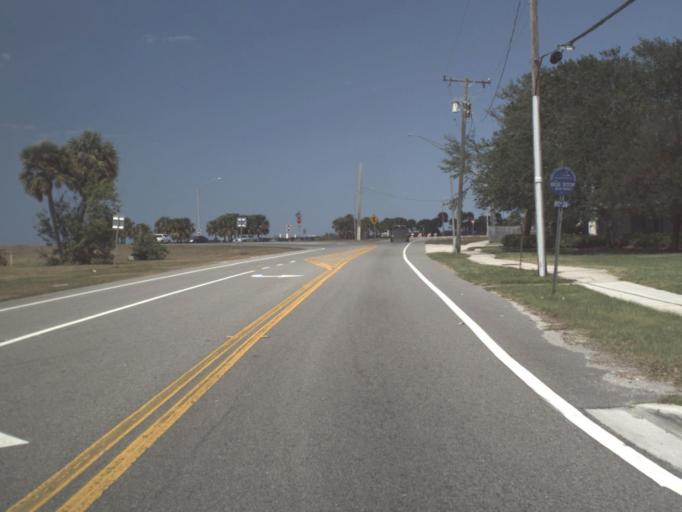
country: US
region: Florida
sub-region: Brevard County
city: Melbourne
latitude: 28.0799
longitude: -80.6012
